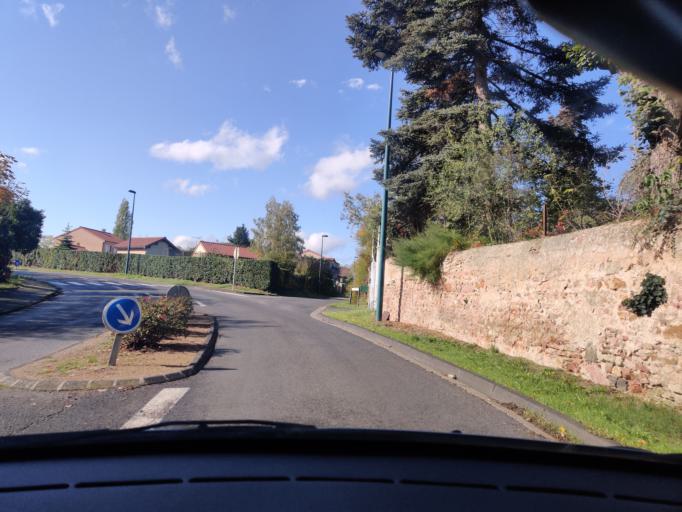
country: FR
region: Auvergne
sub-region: Departement du Puy-de-Dome
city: Combronde
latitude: 45.9940
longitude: 3.1272
